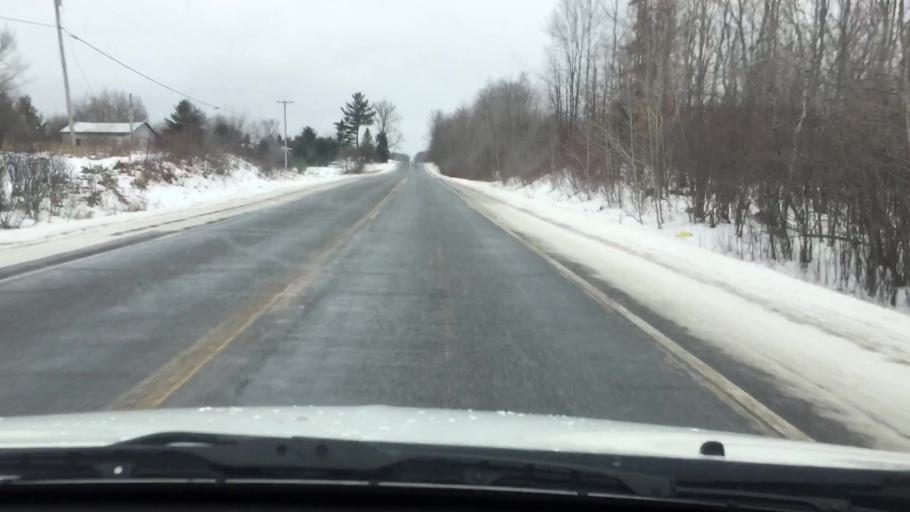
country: US
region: Michigan
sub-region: Wexford County
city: Cadillac
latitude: 44.1127
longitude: -85.4442
